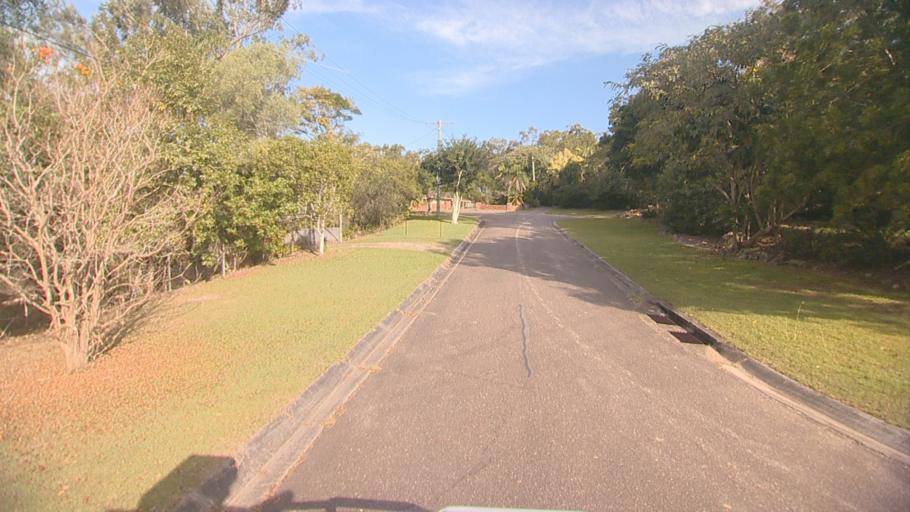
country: AU
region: Queensland
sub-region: Logan
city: Windaroo
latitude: -27.7588
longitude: 153.1965
